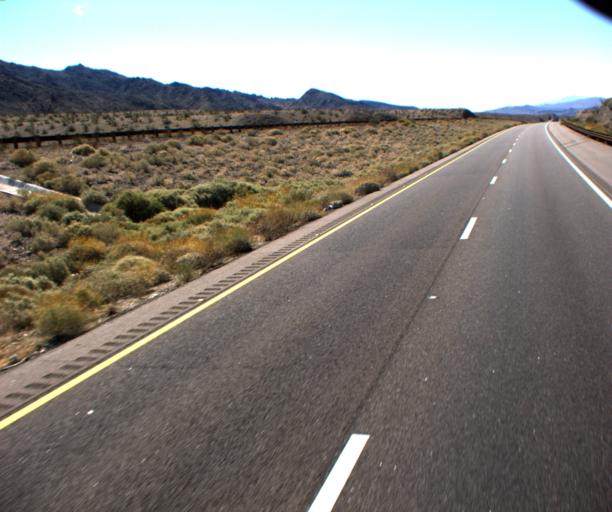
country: US
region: Nevada
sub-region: Clark County
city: Boulder City
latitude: 35.9300
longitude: -114.6351
